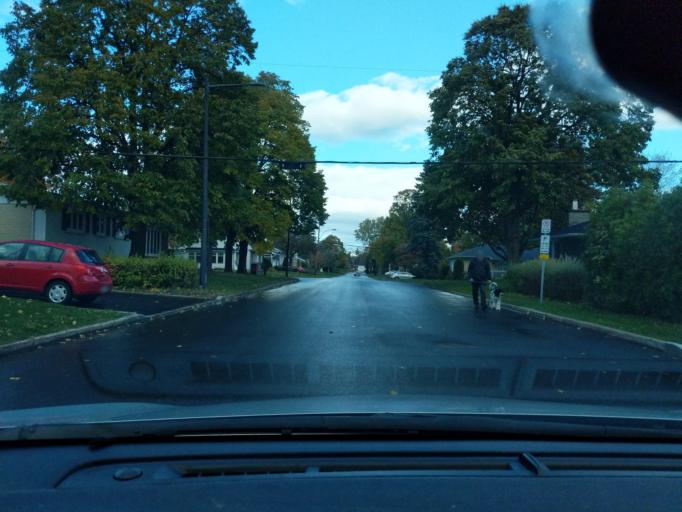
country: CA
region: Quebec
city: L'Ancienne-Lorette
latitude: 46.7630
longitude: -71.2889
